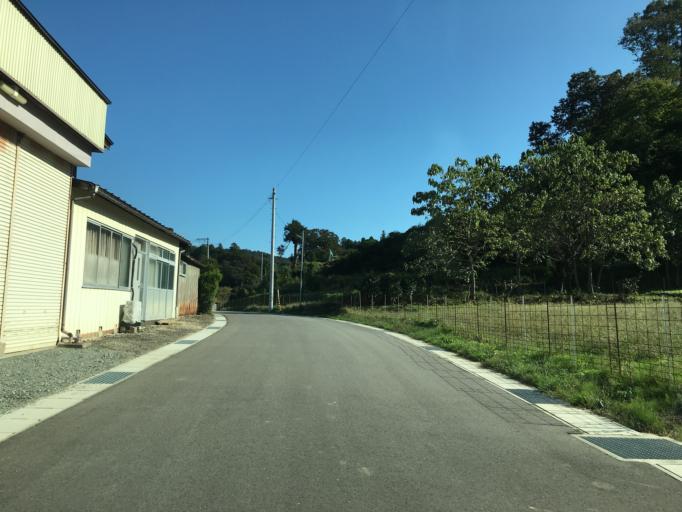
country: JP
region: Fukushima
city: Fukushima-shi
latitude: 37.6685
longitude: 140.5703
